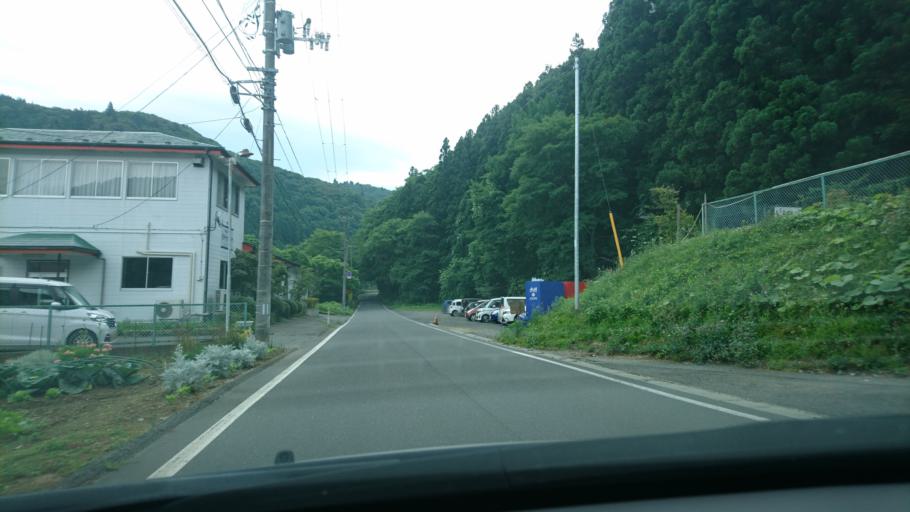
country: JP
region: Iwate
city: Ichinoseki
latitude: 38.8435
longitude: 141.4273
